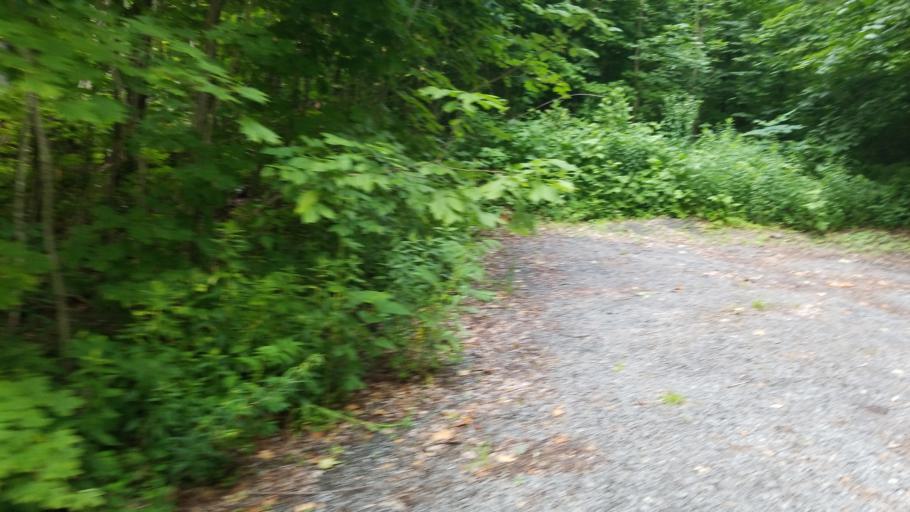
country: US
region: New York
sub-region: St. Lawrence County
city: Gouverneur
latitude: 44.1619
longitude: -75.3717
